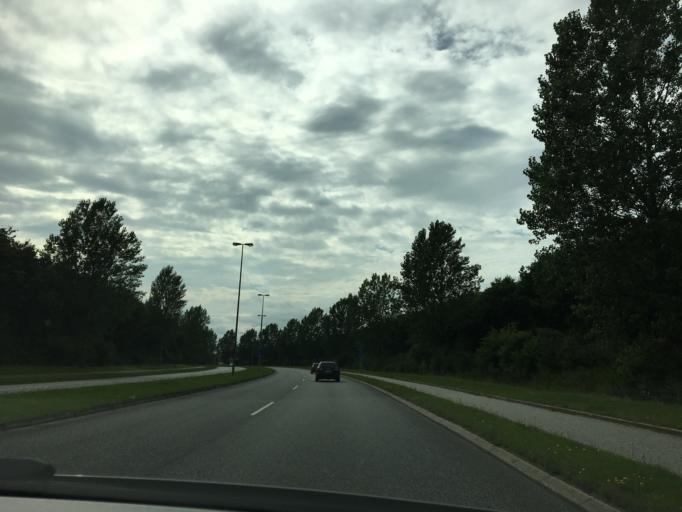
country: DK
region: South Denmark
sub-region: Fredericia Kommune
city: Fredericia
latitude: 55.5873
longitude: 9.7439
